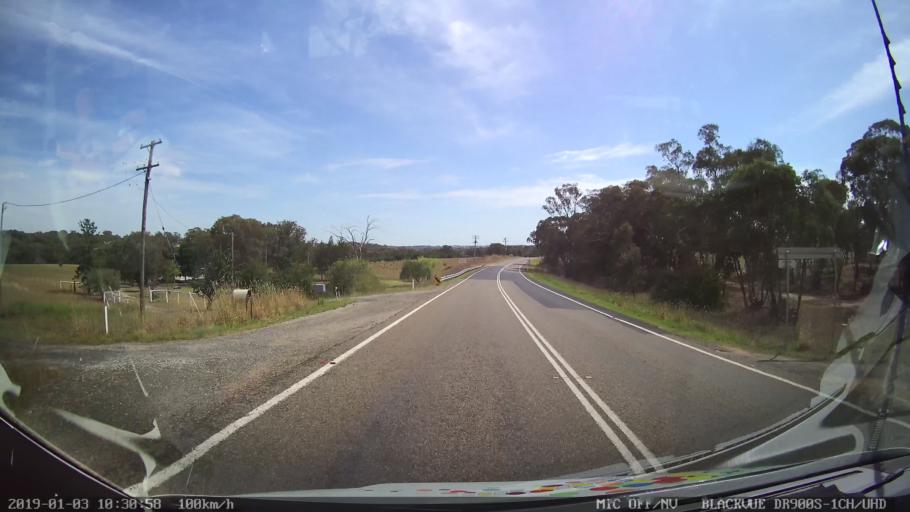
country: AU
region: New South Wales
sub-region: Young
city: Young
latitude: -34.3559
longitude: 148.2727
